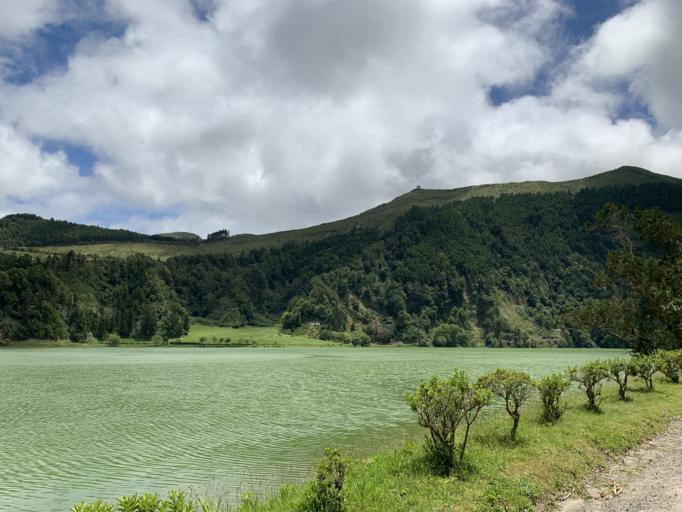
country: PT
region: Azores
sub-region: Ponta Delgada
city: Arrifes
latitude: 37.8508
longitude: -25.7908
